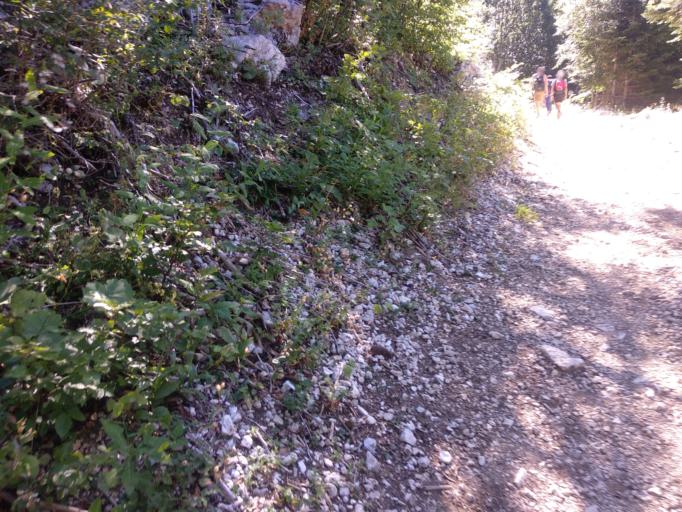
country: FR
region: Rhone-Alpes
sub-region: Departement de l'Isere
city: Le Sappey-en-Chartreuse
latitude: 45.2887
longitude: 5.7766
